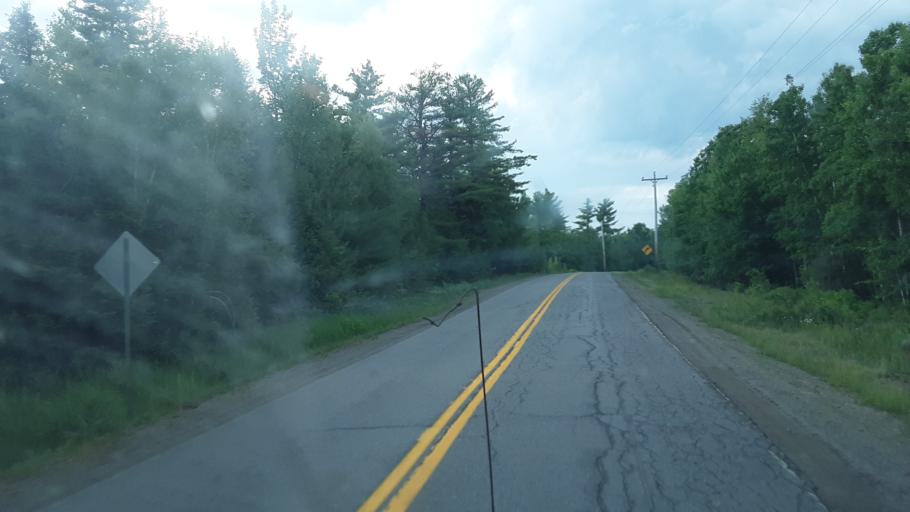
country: US
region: Maine
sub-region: Washington County
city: Calais
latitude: 45.1214
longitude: -67.4991
